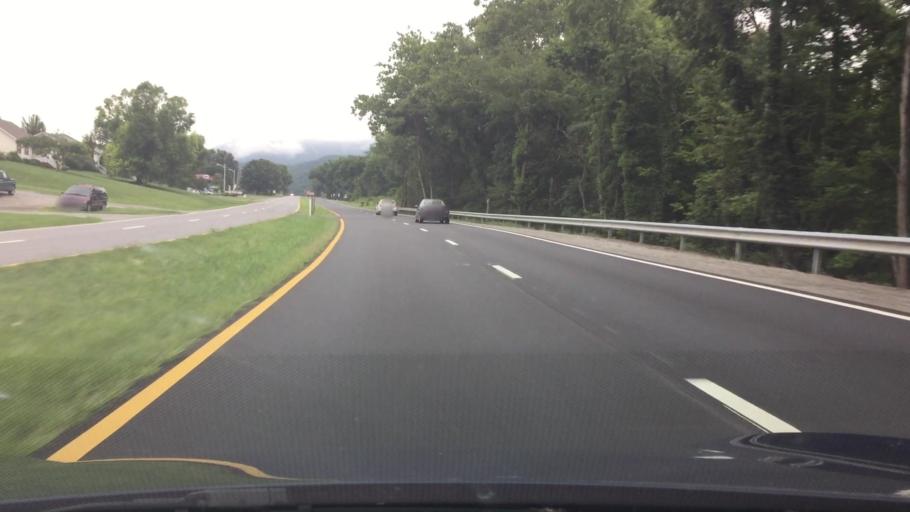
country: US
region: Virginia
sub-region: Montgomery County
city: Shawsville
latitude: 37.1681
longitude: -80.2537
